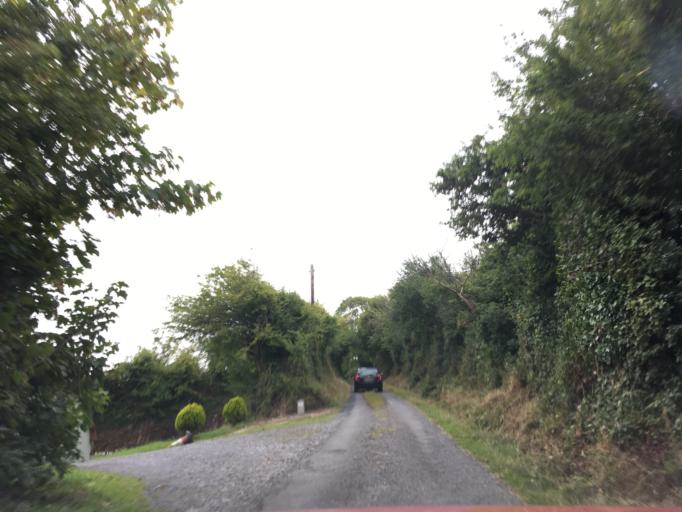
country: IE
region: Munster
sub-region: County Limerick
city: Askeaton
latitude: 52.7166
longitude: -9.0619
